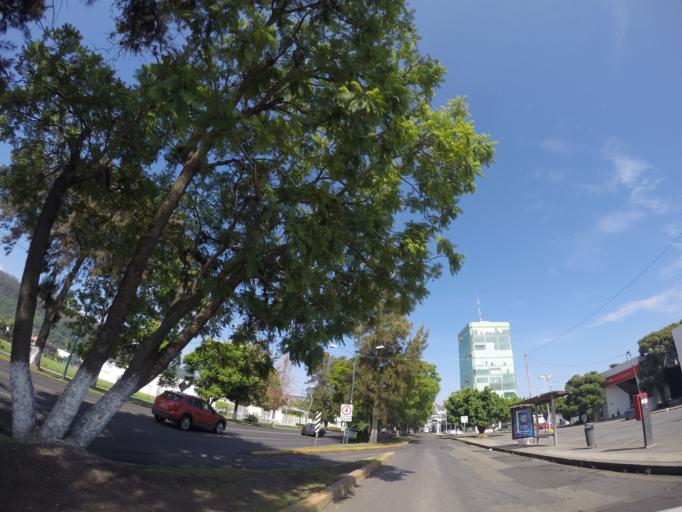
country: MX
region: Michoacan
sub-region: Morelia
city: Puerto de Buenavista (Lazaro Cardenas)
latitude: 19.6875
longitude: -101.1546
